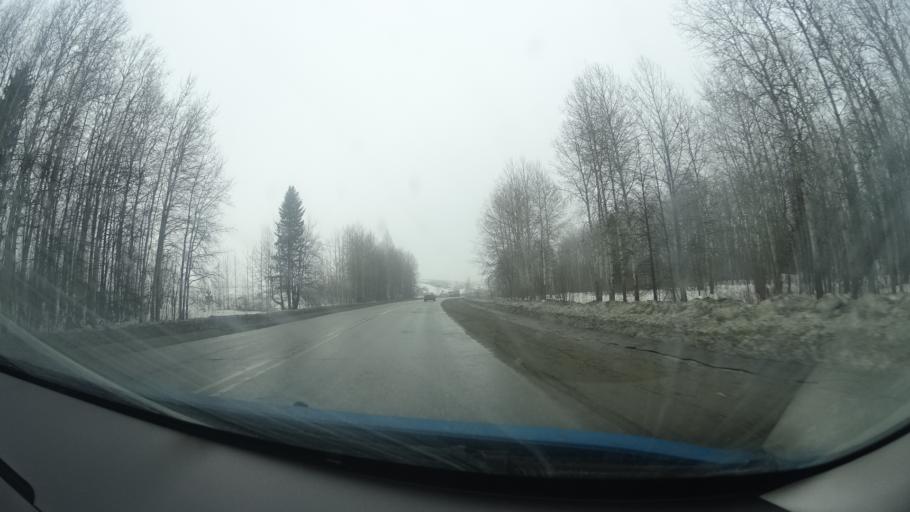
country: RU
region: Perm
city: Kuyeda
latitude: 56.4585
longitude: 55.6275
